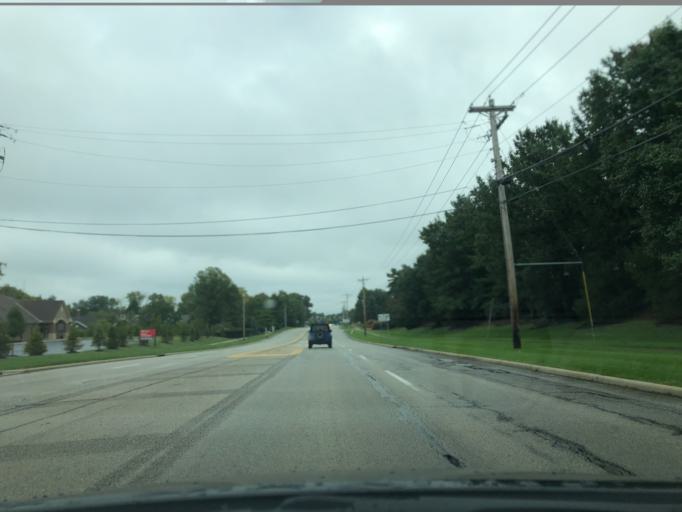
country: US
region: Ohio
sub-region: Hamilton County
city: Sixteen Mile Stand
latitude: 39.2752
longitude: -84.3337
